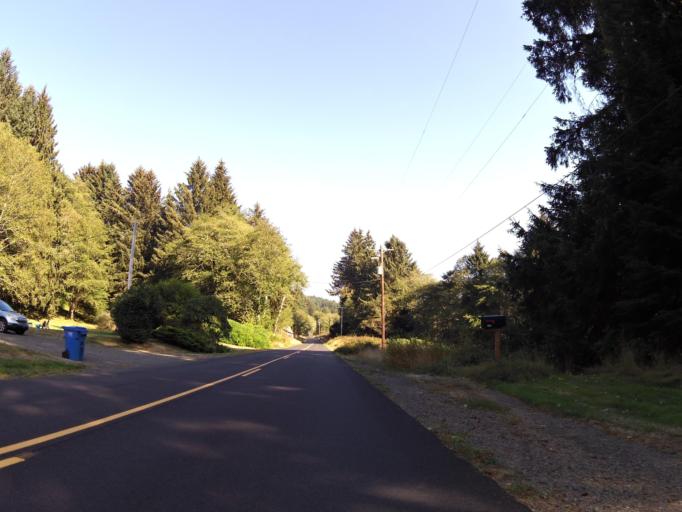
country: US
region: Oregon
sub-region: Lincoln County
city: Rose Lodge
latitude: 45.0756
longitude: -123.9339
